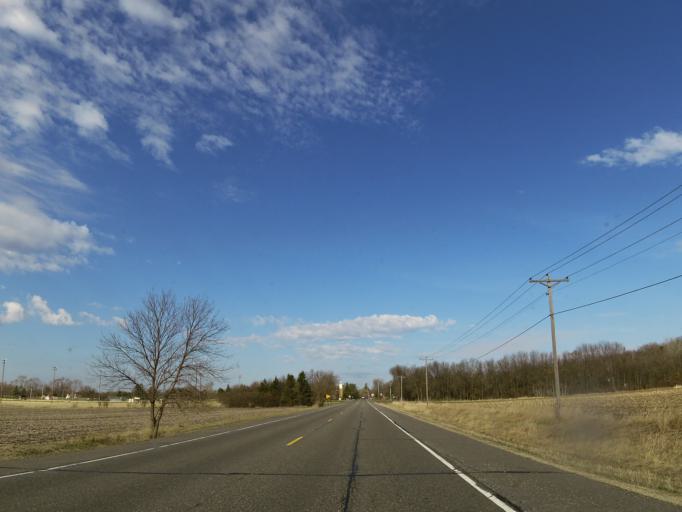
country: US
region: Minnesota
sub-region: Washington County
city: Cottage Grove
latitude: 44.8479
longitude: -92.8753
